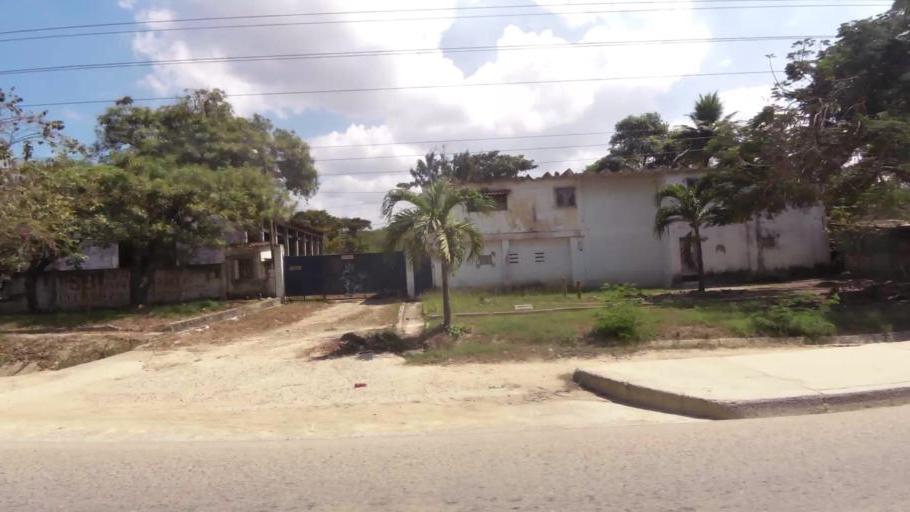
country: CO
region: Bolivar
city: Cartagena
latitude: 10.3676
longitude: -75.5077
